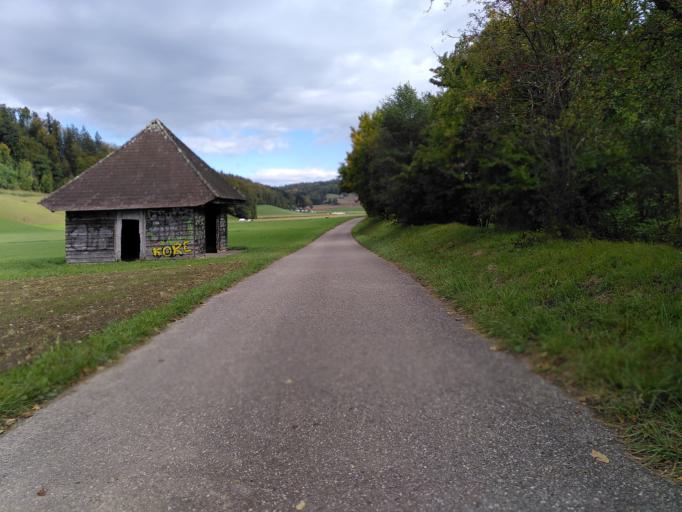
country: CH
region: Bern
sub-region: Emmental District
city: Wynigen
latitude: 47.1179
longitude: 7.6694
